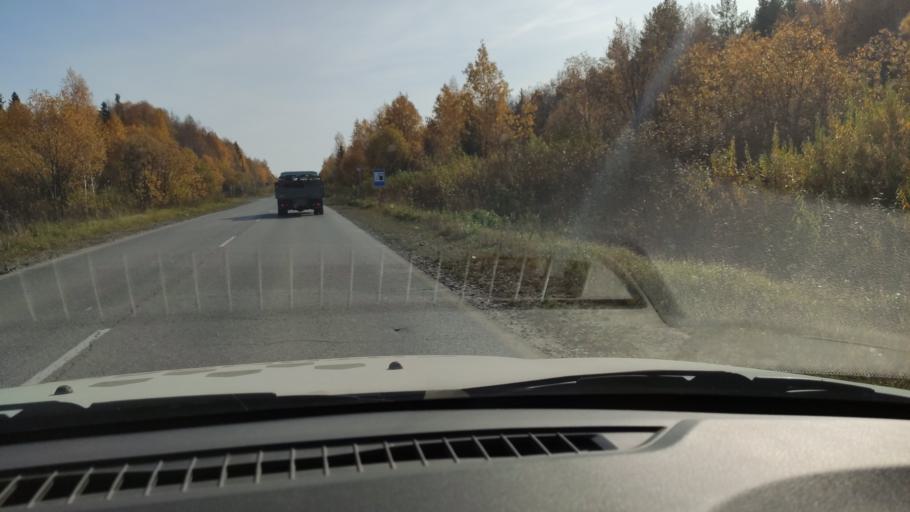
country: RU
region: Perm
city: Novyye Lyady
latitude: 58.0314
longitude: 56.6161
